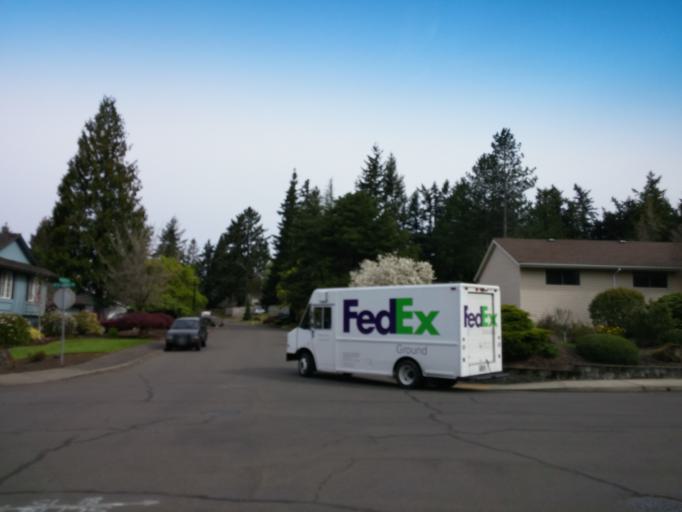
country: US
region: Oregon
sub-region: Washington County
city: Cedar Mill
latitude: 45.5385
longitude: -122.8002
